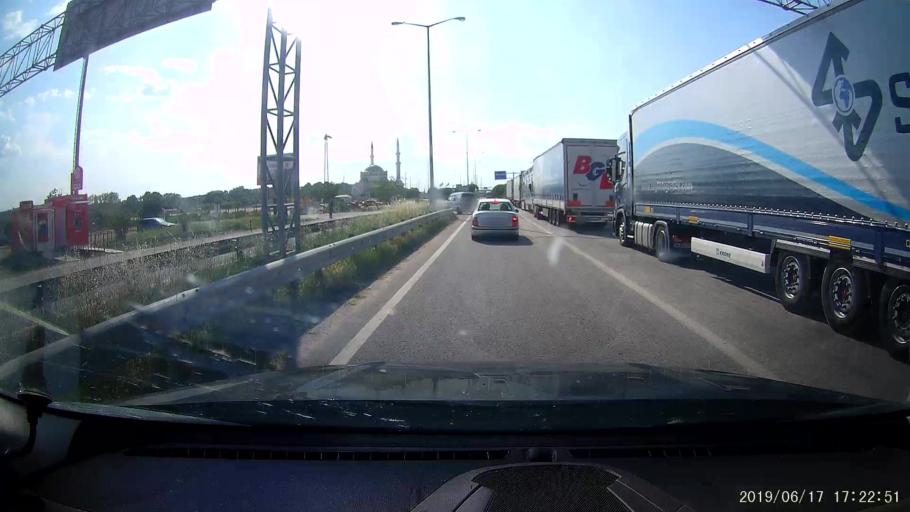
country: GR
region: East Macedonia and Thrace
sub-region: Nomos Evrou
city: Rizia
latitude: 41.7131
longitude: 26.3692
